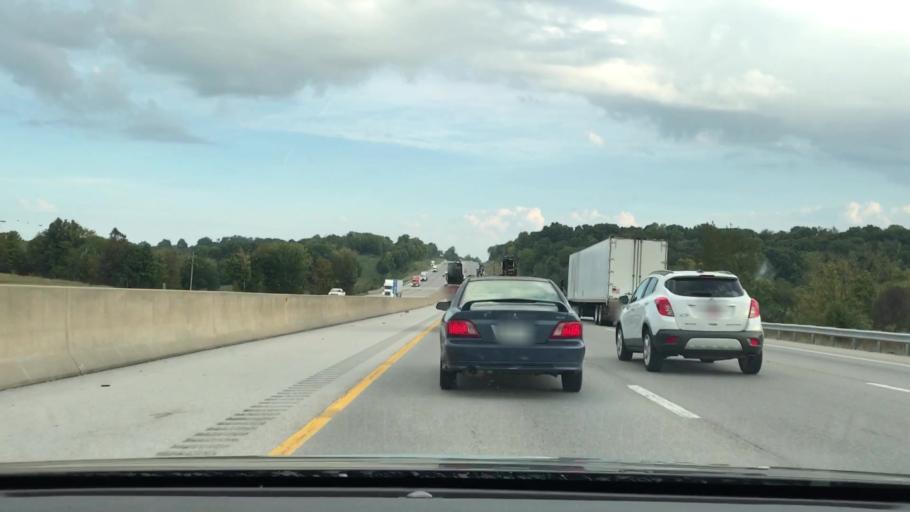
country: US
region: Kentucky
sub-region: Warren County
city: Plano
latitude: 36.8059
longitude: -86.4740
